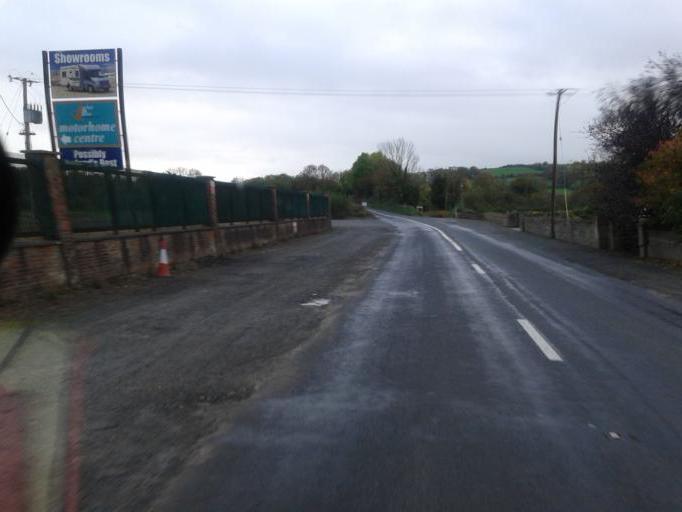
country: IE
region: Munster
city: Ballina
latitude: 52.7745
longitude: -8.4309
